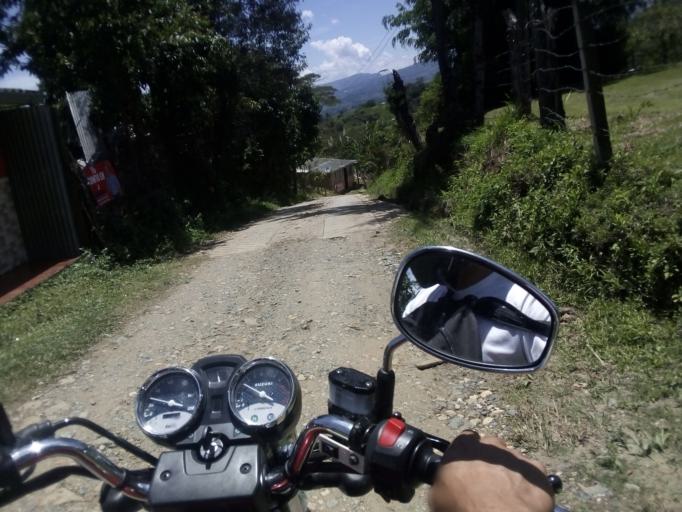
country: CO
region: Santander
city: Guepsa
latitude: 6.0124
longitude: -73.5547
